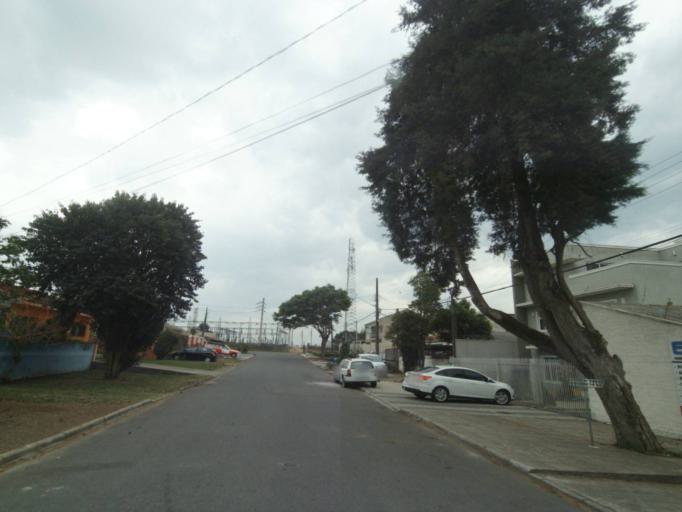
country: BR
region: Parana
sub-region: Pinhais
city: Pinhais
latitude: -25.4795
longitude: -49.2077
